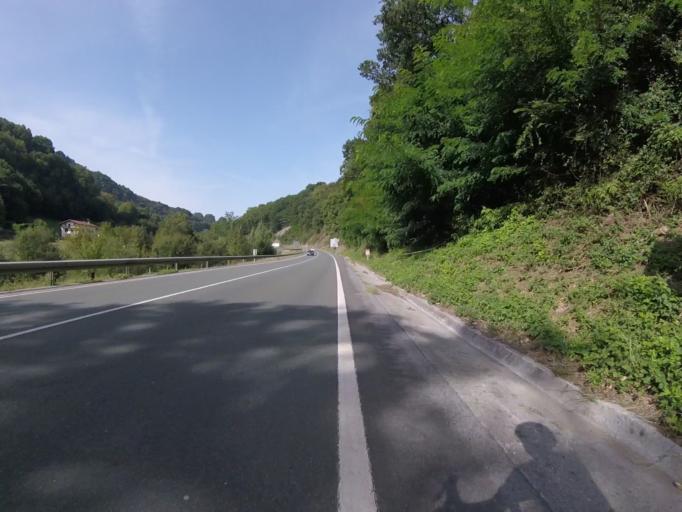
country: ES
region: Navarre
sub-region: Provincia de Navarra
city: Doneztebe
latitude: 43.1429
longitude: -1.5833
